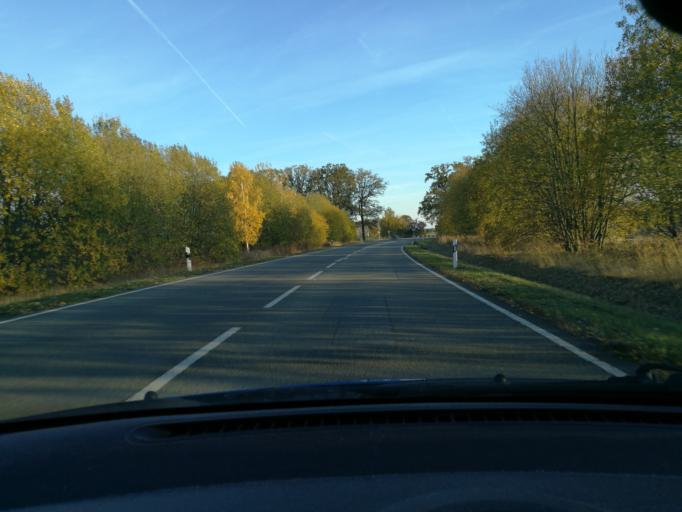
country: DE
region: Brandenburg
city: Perleberg
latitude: 53.0823
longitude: 11.8820
